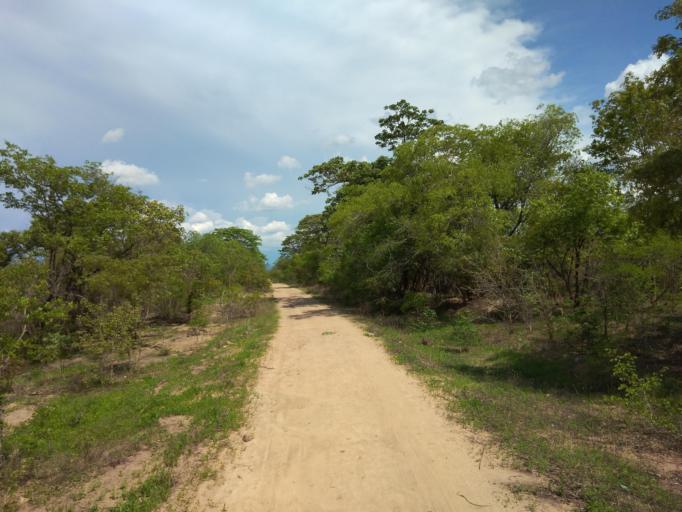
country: ZM
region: Eastern
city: Nyimba
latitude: -14.1158
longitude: 30.1286
